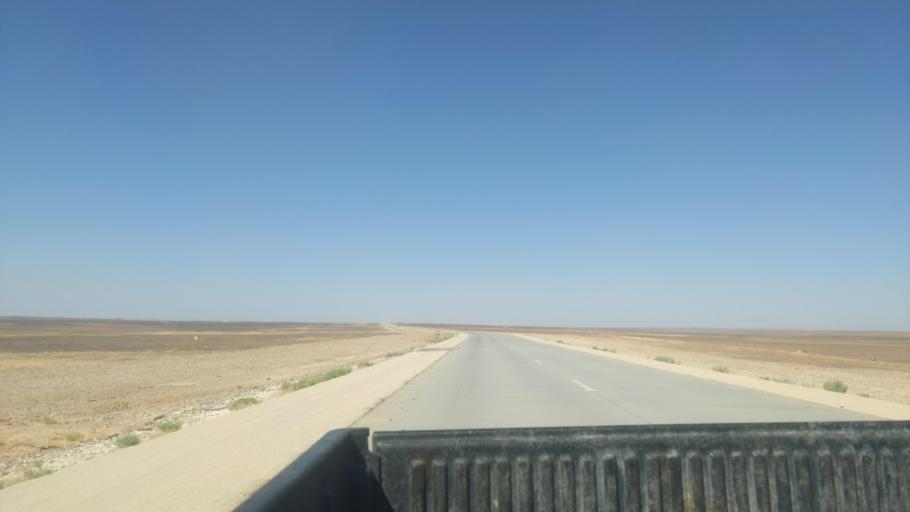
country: JO
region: Amman
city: Al Azraq ash Shamali
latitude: 31.4493
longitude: 36.7683
